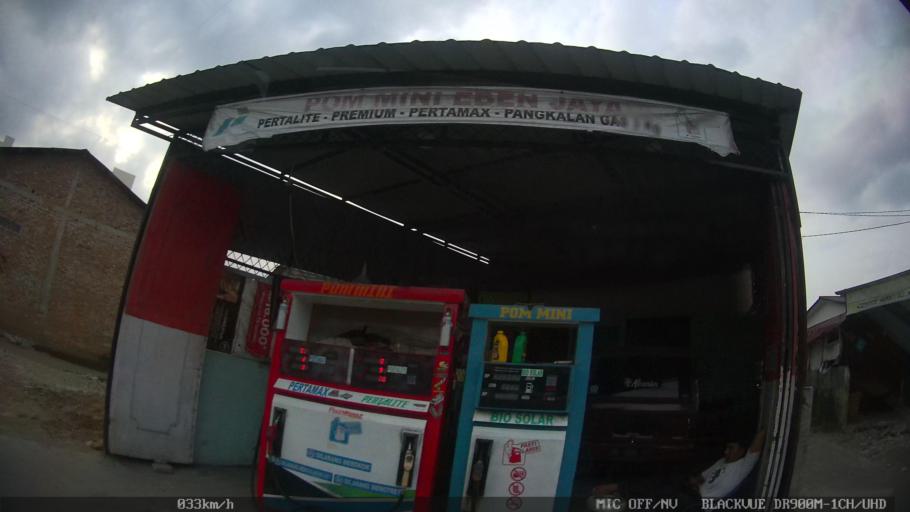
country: ID
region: North Sumatra
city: Sunggal
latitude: 3.5642
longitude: 98.6058
